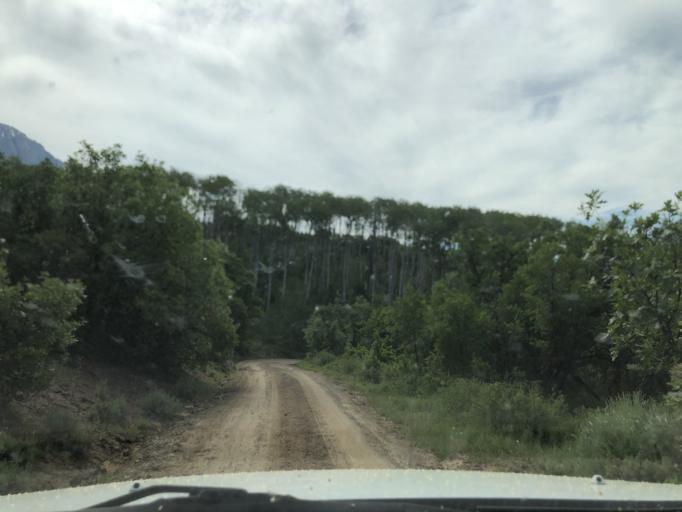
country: US
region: Colorado
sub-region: Delta County
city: Paonia
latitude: 39.0301
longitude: -107.3434
